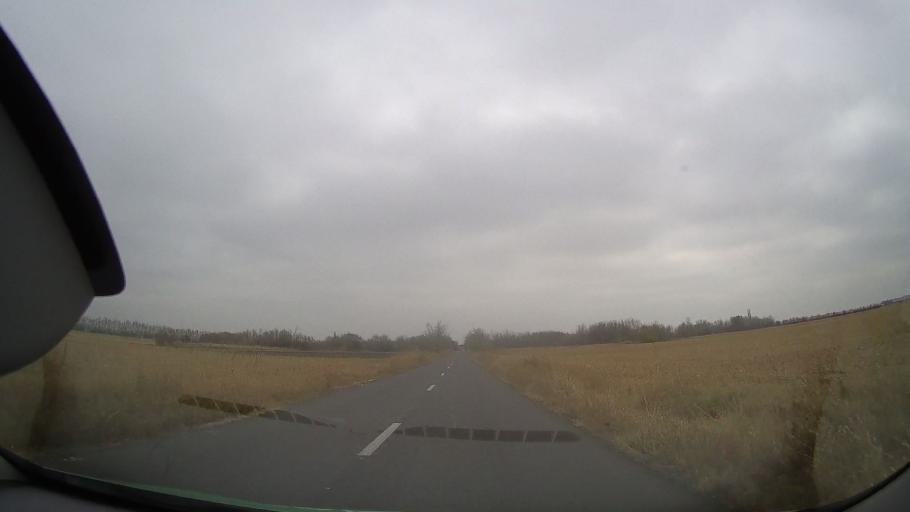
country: RO
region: Buzau
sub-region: Comuna Bradeanu
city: Bradeanu
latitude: 44.8858
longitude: 26.8754
